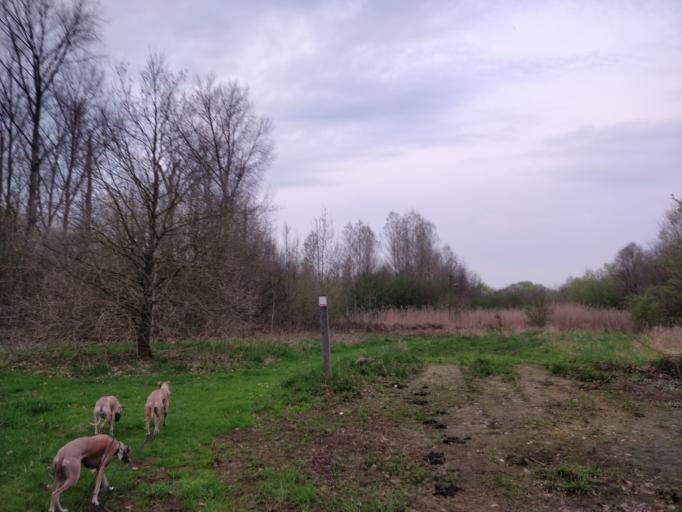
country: BE
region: Flanders
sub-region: Provincie Antwerpen
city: Rumst
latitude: 51.0744
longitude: 4.4382
